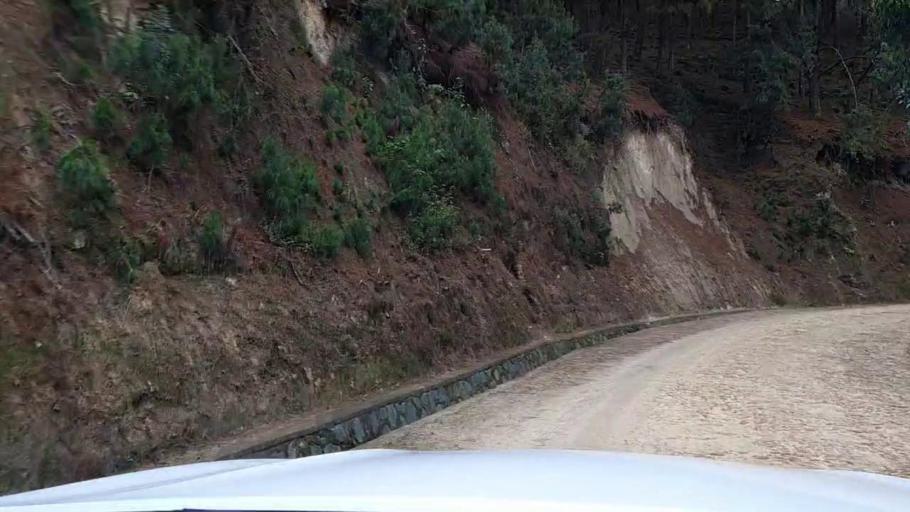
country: RW
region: Southern Province
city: Nzega
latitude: -2.3815
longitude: 29.3828
